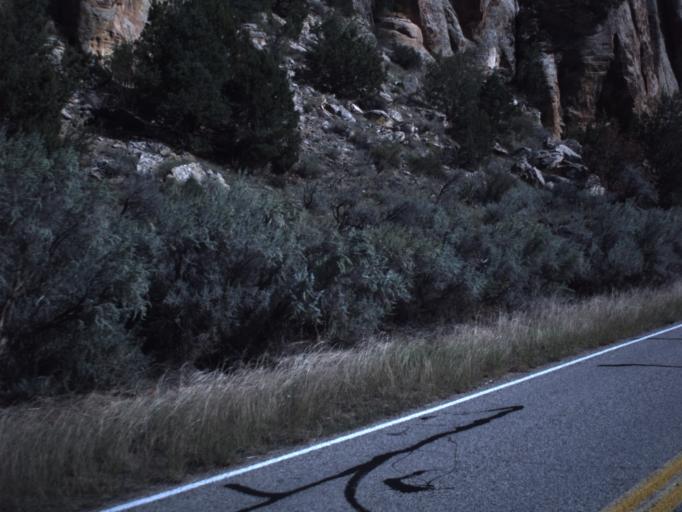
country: US
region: Utah
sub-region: San Juan County
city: Monticello
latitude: 37.9989
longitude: -109.5301
